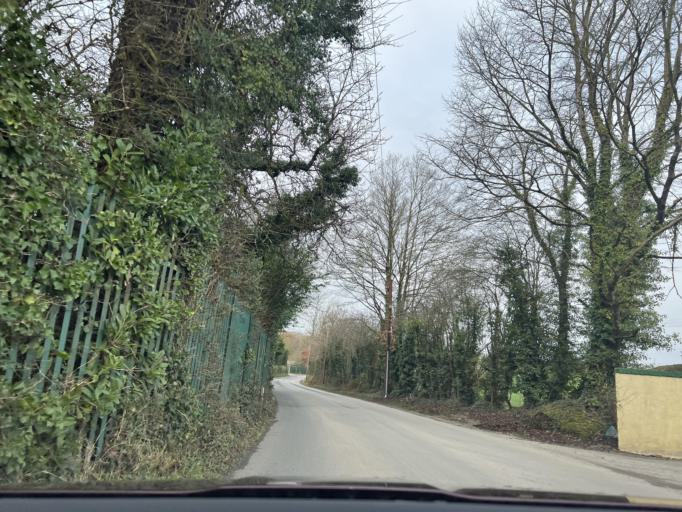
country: IE
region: Leinster
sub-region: Loch Garman
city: Castlebridge
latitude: 52.3828
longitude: -6.5610
